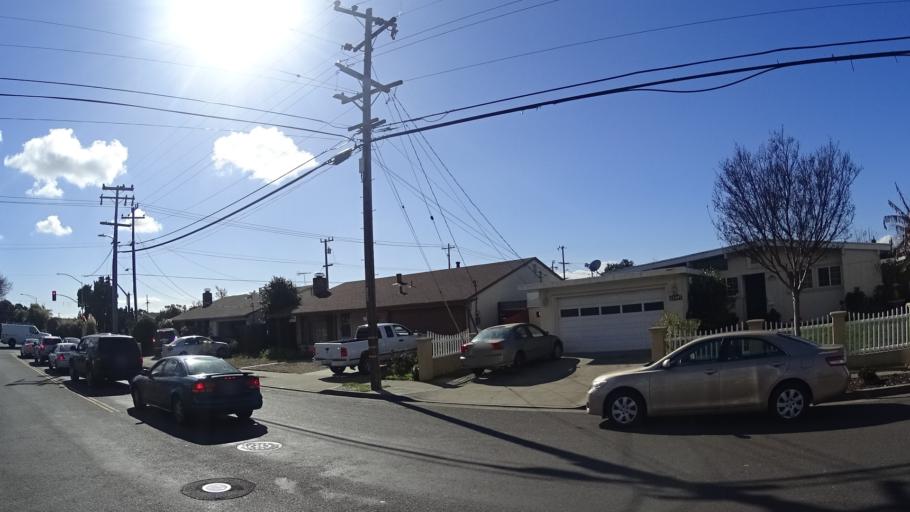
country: US
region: California
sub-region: Alameda County
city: Cherryland
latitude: 37.6547
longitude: -122.1075
